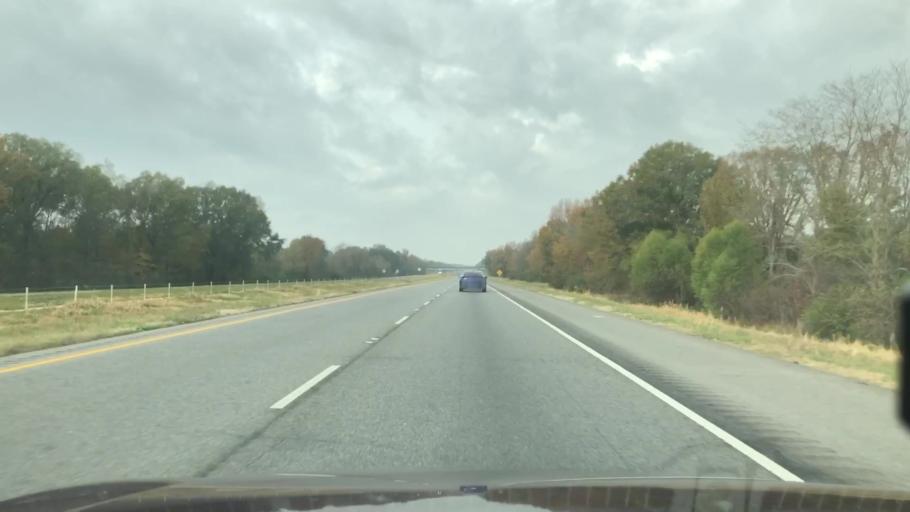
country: US
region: Louisiana
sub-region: Richland Parish
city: Delhi
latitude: 32.4452
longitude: -91.5160
